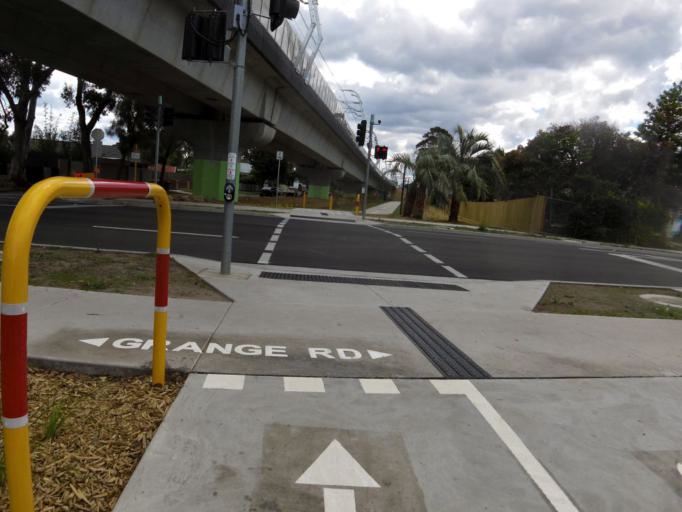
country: AU
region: Victoria
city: Glen Huntly
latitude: -37.8818
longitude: 145.0494
